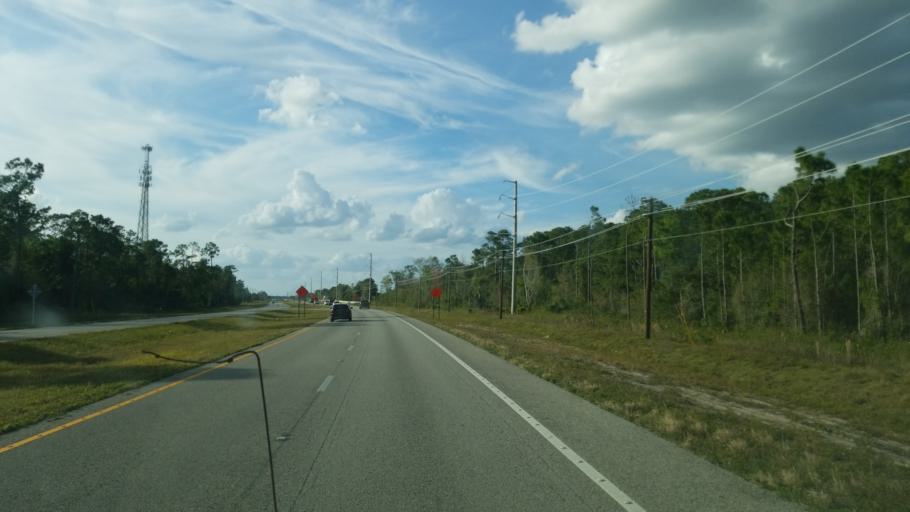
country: US
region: Florida
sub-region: Osceola County
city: Saint Cloud
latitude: 28.1835
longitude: -81.1383
